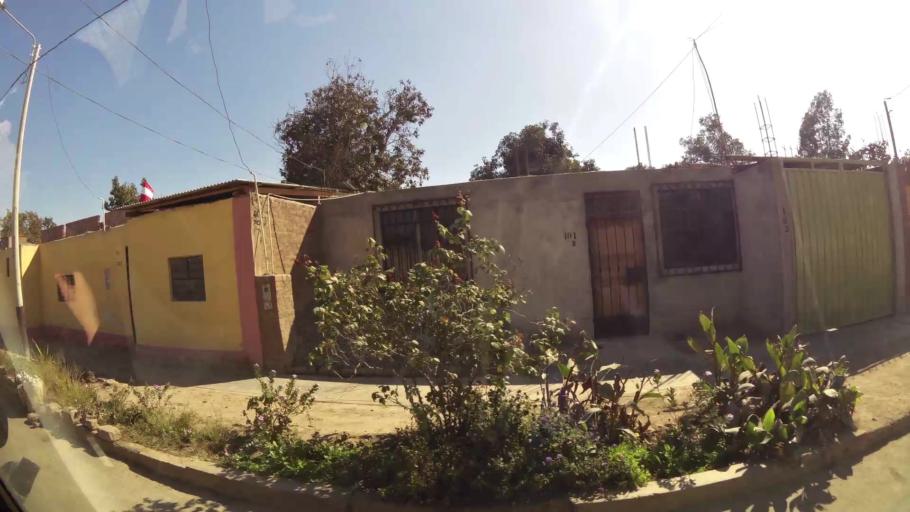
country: PE
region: Ica
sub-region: Provincia de Ica
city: La Tinguina
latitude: -14.0367
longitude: -75.7125
